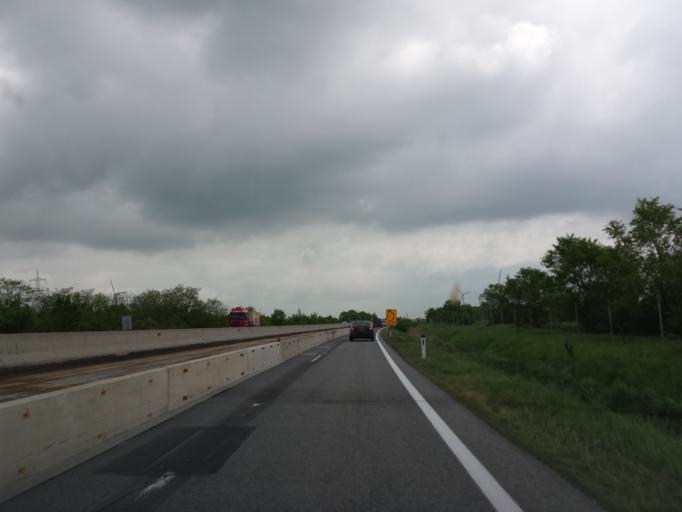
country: AT
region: Burgenland
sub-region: Politischer Bezirk Neusiedl am See
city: Parndorf
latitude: 47.9700
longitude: 16.8780
